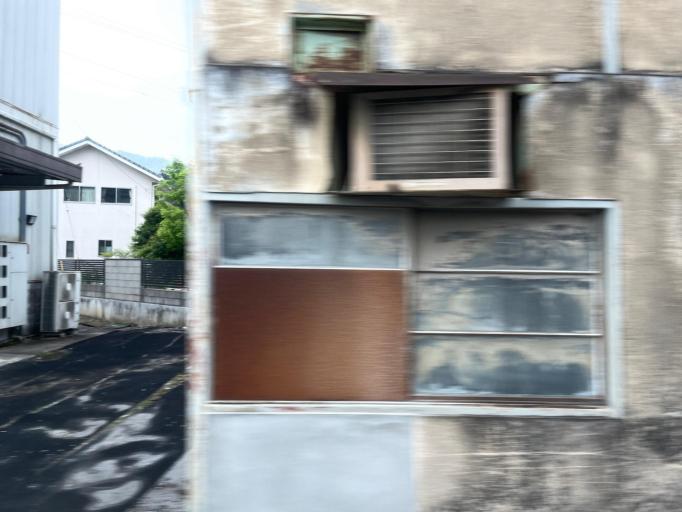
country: JP
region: Tochigi
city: Tanuma
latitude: 36.4557
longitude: 139.6376
